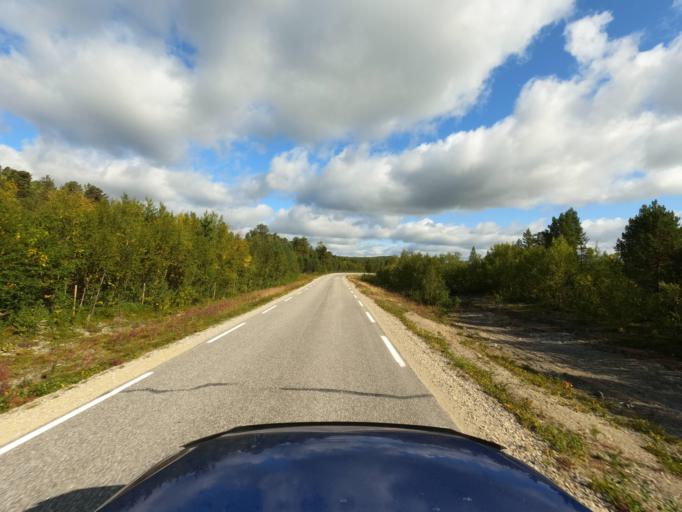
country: NO
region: Finnmark Fylke
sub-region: Karasjok
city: Karasjohka
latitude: 69.4295
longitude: 24.9549
